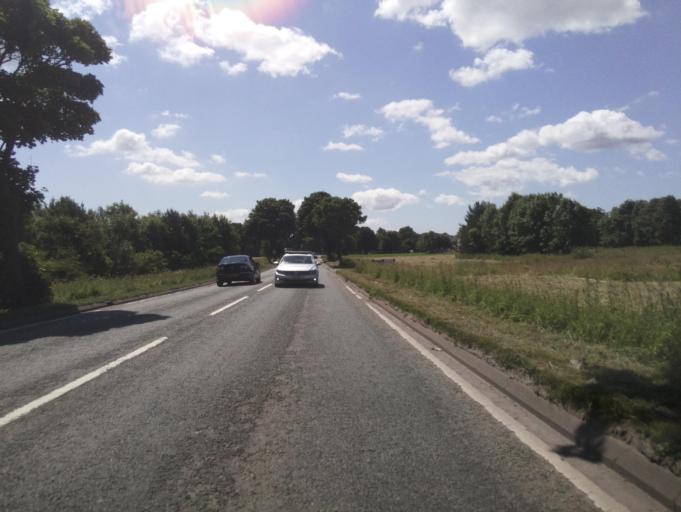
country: GB
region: England
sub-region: Derbyshire
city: Buxton
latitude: 53.2663
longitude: -1.8983
